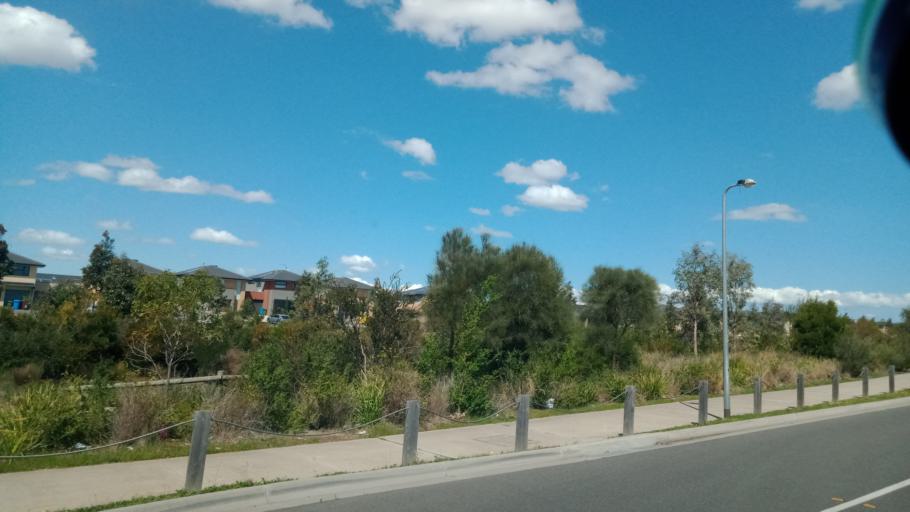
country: AU
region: Victoria
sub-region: Casey
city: Cranbourne West
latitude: -38.0984
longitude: 145.2487
